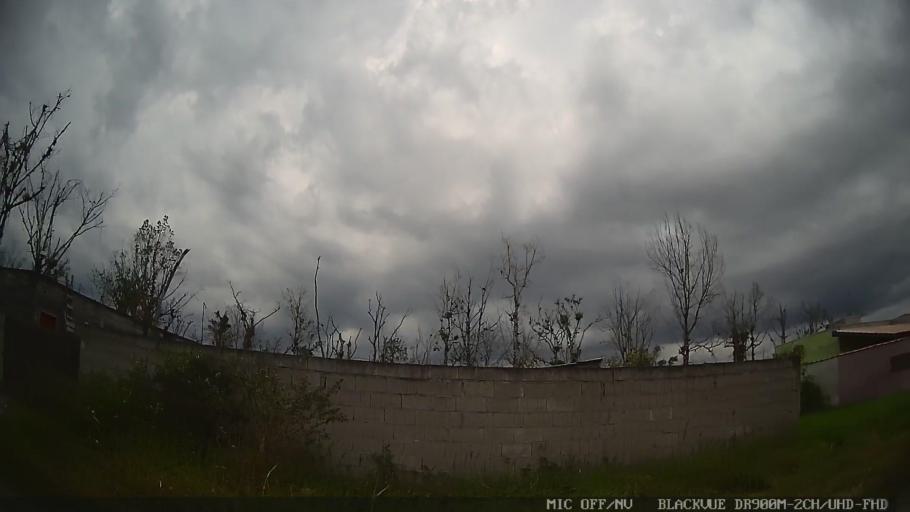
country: BR
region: Sao Paulo
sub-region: Caraguatatuba
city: Caraguatatuba
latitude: -23.6745
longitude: -45.4543
